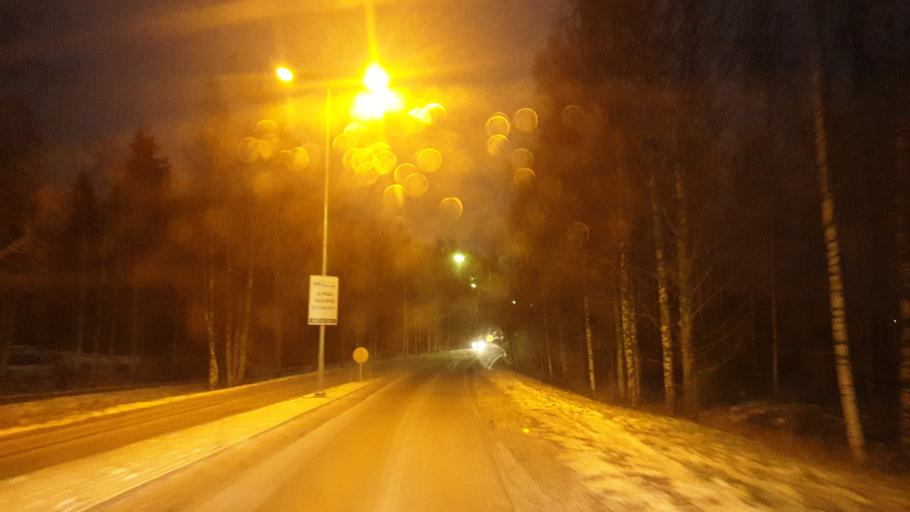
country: FI
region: Southern Savonia
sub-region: Savonlinna
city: Savonlinna
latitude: 61.8650
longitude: 28.9425
